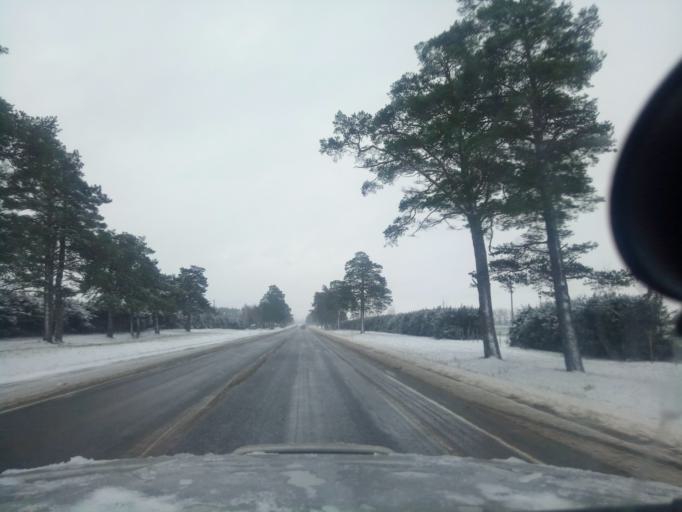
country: BY
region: Minsk
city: Nyasvizh
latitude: 53.2509
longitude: 26.6208
